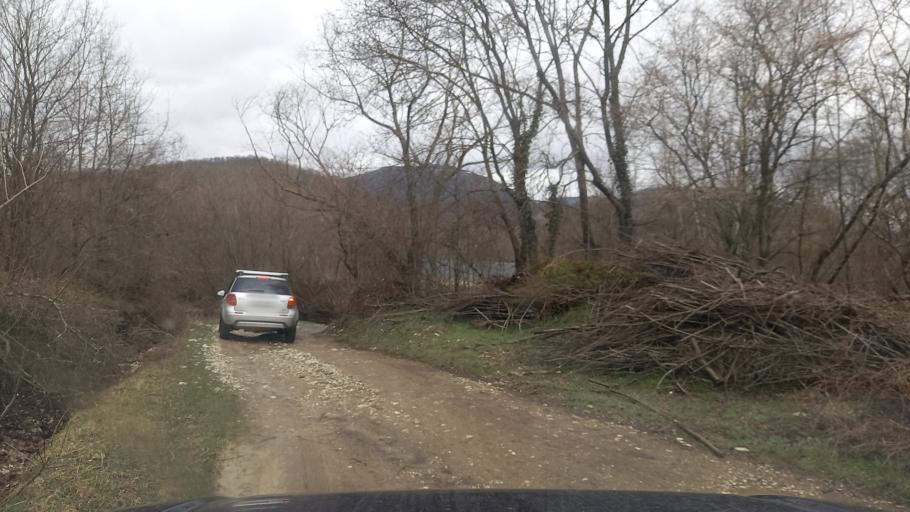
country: RU
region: Krasnodarskiy
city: Pshada
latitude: 44.4813
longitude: 38.4072
